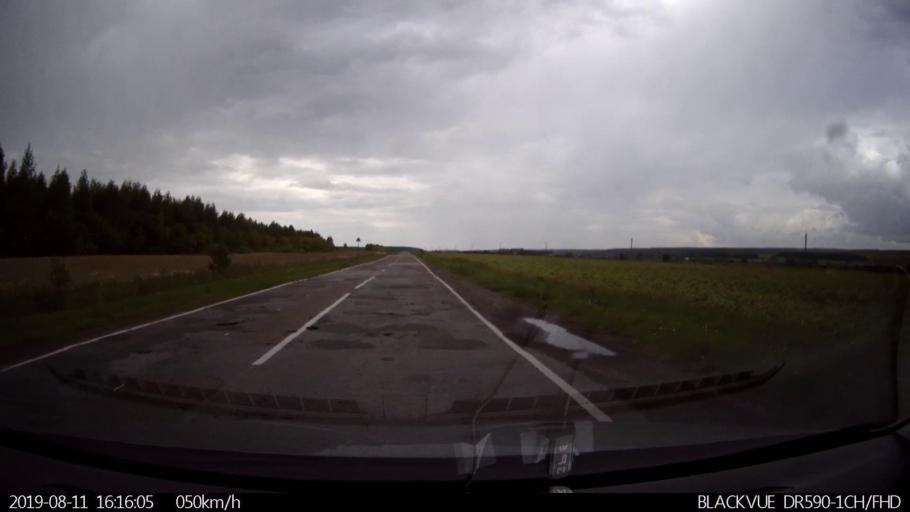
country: RU
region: Ulyanovsk
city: Mayna
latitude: 54.0385
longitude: 47.6231
